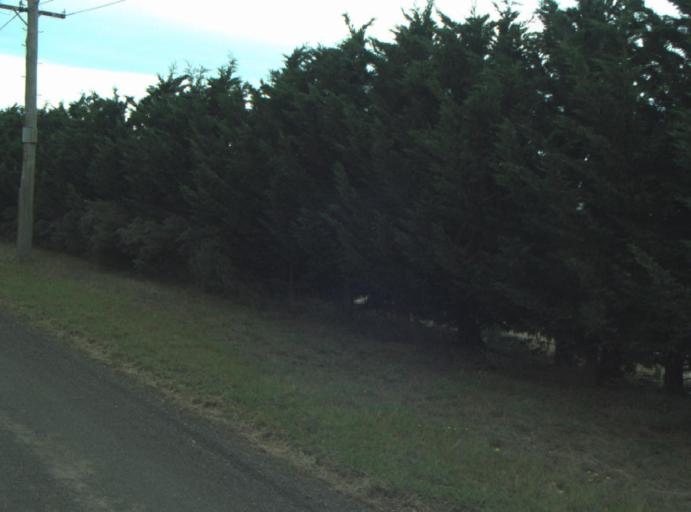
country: AU
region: Victoria
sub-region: Greater Geelong
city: Clifton Springs
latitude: -38.2182
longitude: 144.5779
